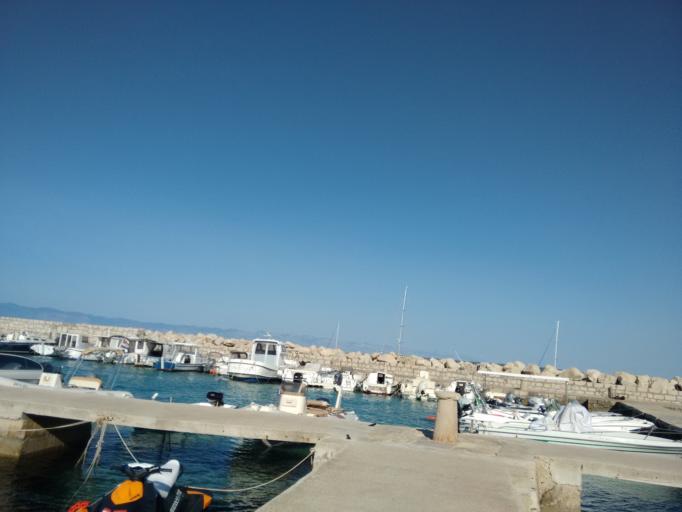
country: HR
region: Licko-Senjska
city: Novalja
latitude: 44.3743
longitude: 14.7020
